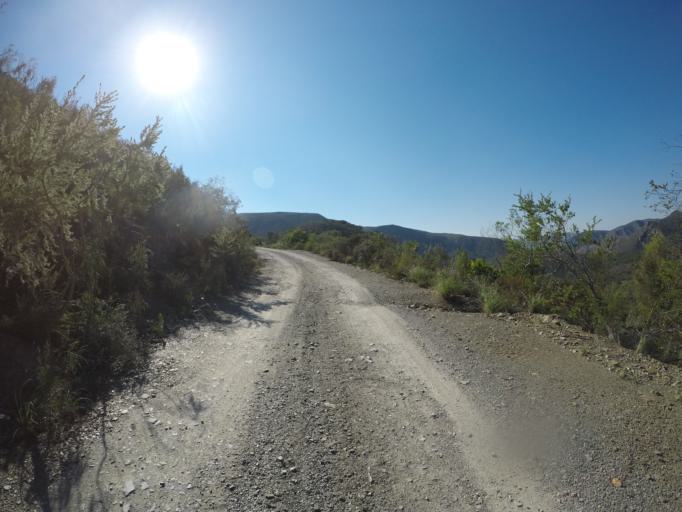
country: ZA
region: Eastern Cape
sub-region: Cacadu District Municipality
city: Kareedouw
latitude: -33.6548
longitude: 24.5077
